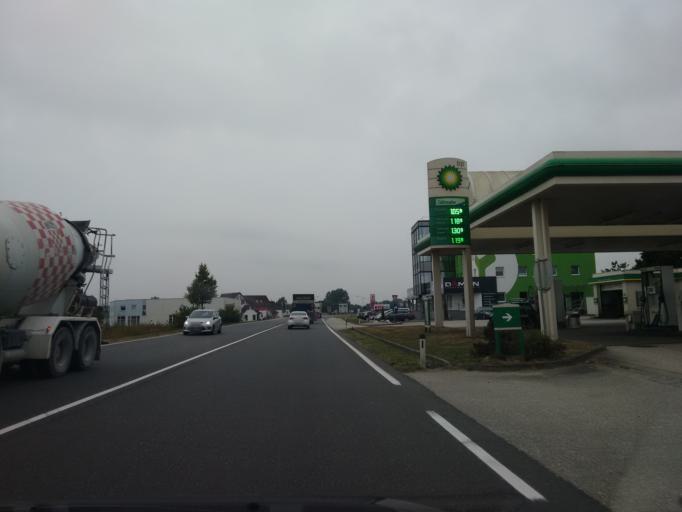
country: AT
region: Upper Austria
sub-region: Wels-Land
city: Marchtrenk
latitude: 48.1915
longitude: 14.1219
